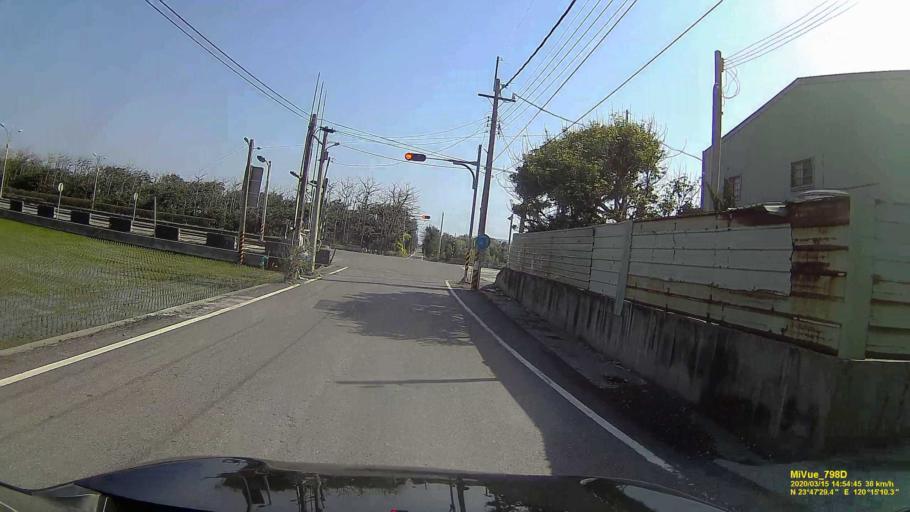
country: TW
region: Taiwan
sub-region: Yunlin
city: Douliu
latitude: 23.7916
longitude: 120.2528
